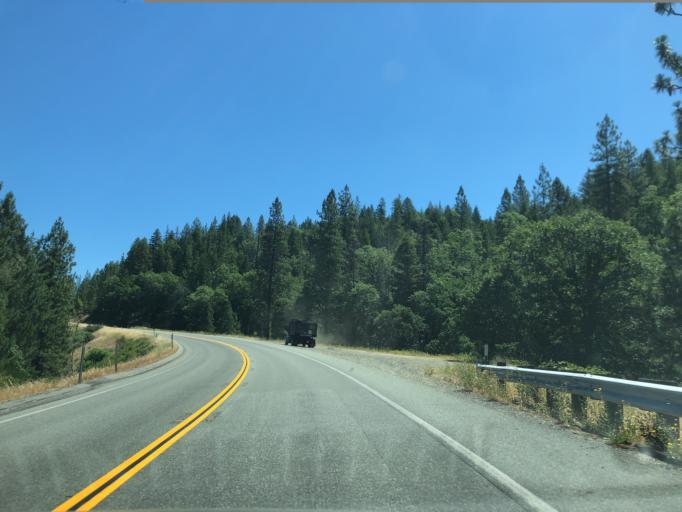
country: US
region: California
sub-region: Trinity County
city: Lewiston
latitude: 40.6698
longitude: -122.8686
